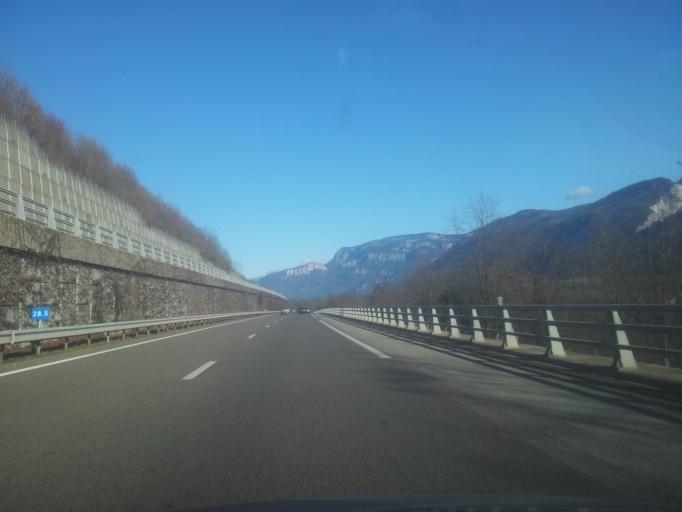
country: FR
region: Rhone-Alpes
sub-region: Departement de l'Isere
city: Saint-Sauveur
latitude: 45.1649
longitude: 5.3707
